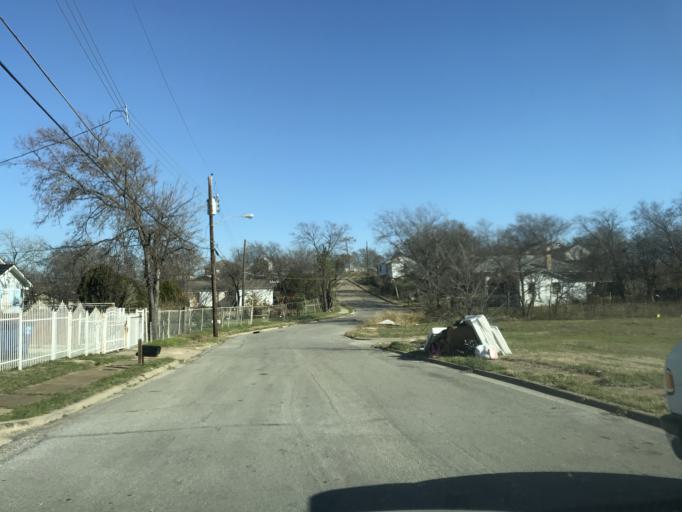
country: US
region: Texas
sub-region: Dallas County
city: Cockrell Hill
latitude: 32.7673
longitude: -96.9067
